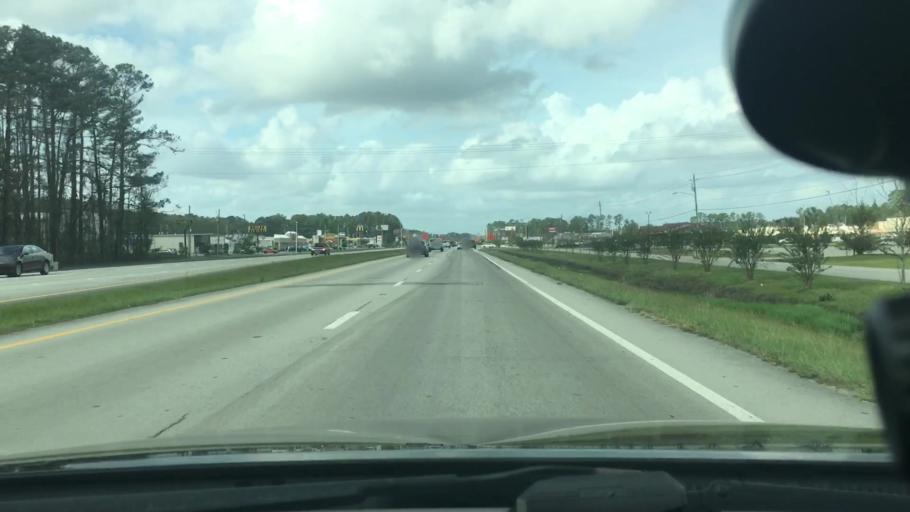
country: US
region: North Carolina
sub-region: Craven County
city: Havelock
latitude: 34.9060
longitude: -76.9340
